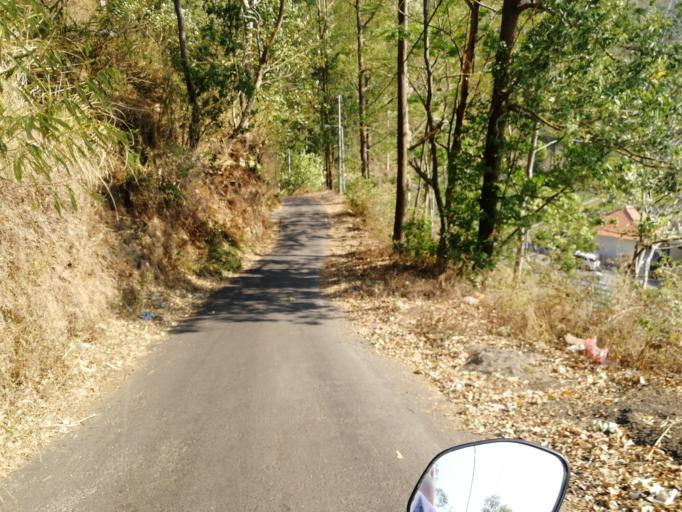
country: ID
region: Bali
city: Banjar Trunyan
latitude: -8.2582
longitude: 115.4238
